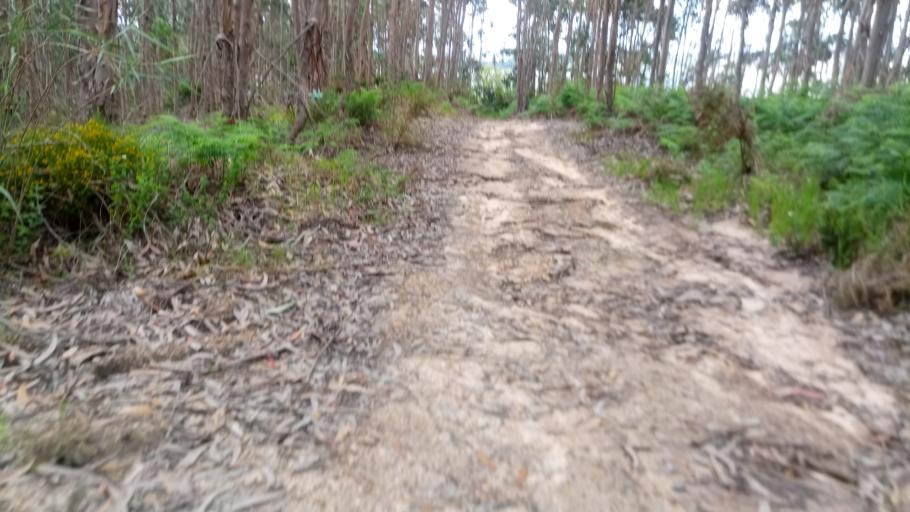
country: PT
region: Leiria
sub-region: Obidos
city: Obidos
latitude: 39.3925
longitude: -9.2090
